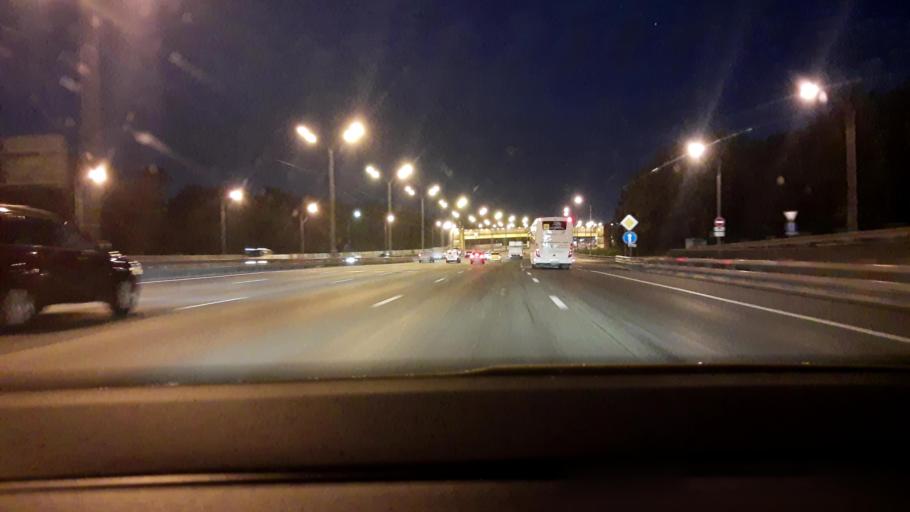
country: RU
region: Moskovskaya
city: Levoberezhnaya
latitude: 55.8851
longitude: 37.4711
